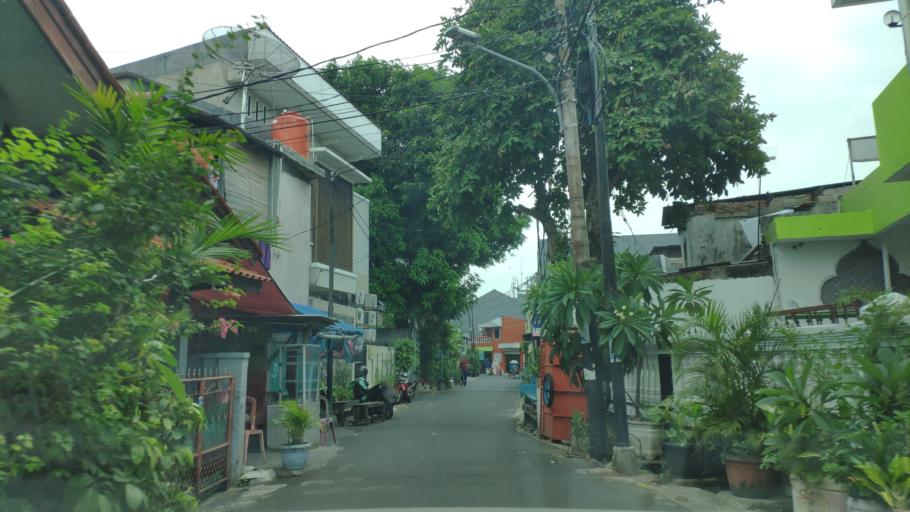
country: ID
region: Jakarta Raya
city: Jakarta
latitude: -6.1909
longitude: 106.8012
